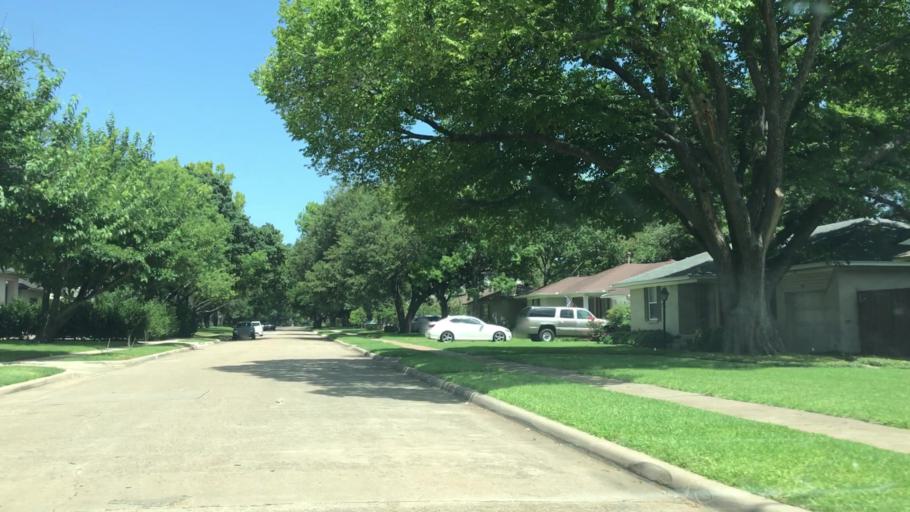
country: US
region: Texas
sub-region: Dallas County
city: University Park
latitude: 32.8727
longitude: -96.8418
